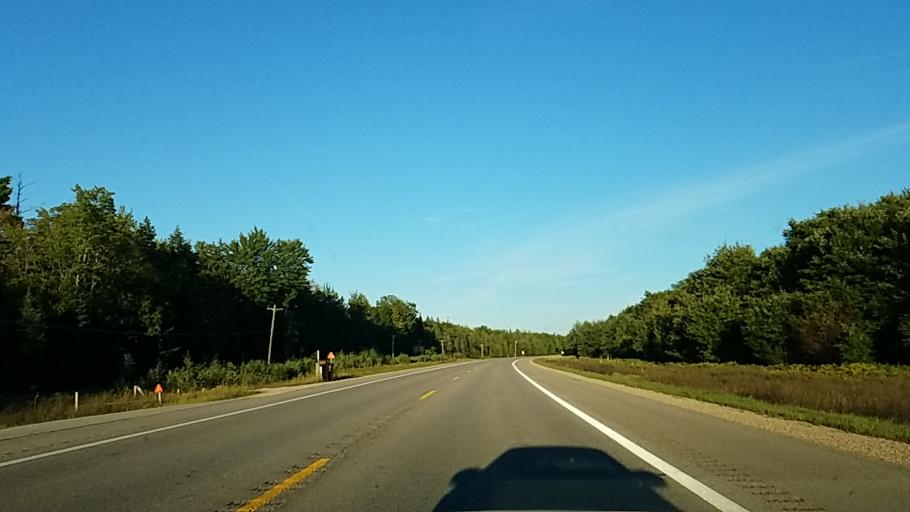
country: US
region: Michigan
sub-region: Alger County
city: Munising
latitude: 46.4425
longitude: -86.7367
